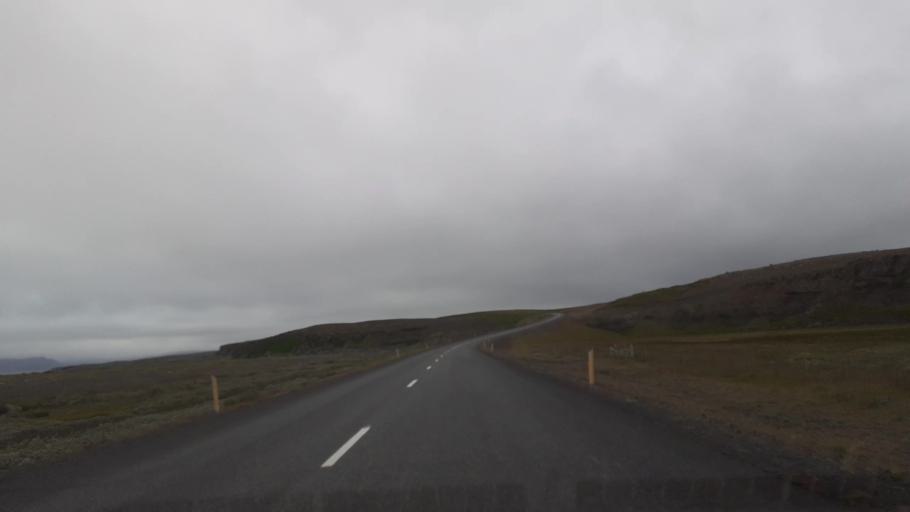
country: IS
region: Northeast
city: Husavik
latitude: 66.2045
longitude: -16.4703
